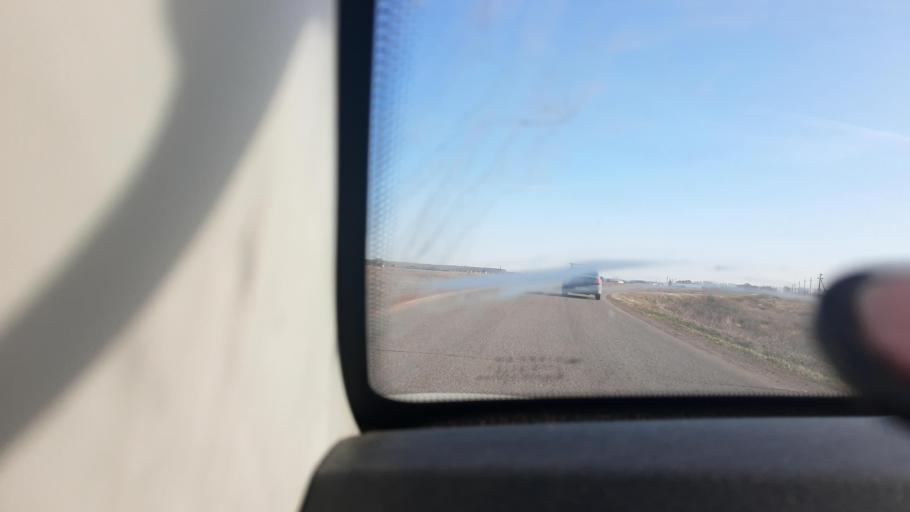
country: RU
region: Bashkortostan
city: Asanovo
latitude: 54.9459
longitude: 55.5208
